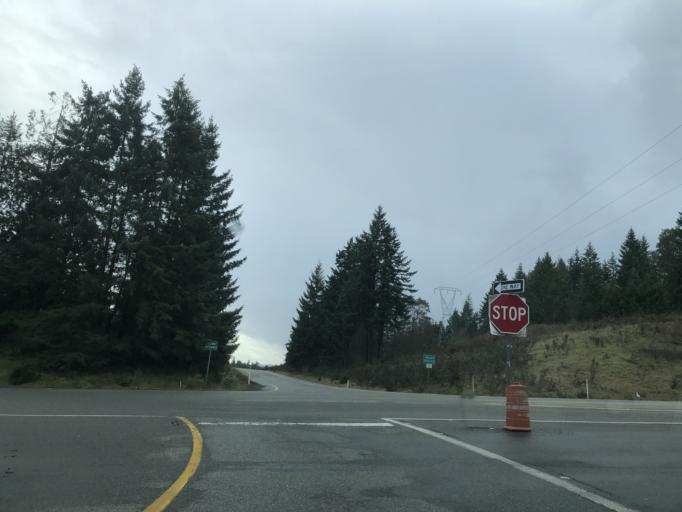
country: US
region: Washington
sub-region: Kitsap County
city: Bangor Trident Base
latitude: 47.7014
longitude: -122.6858
